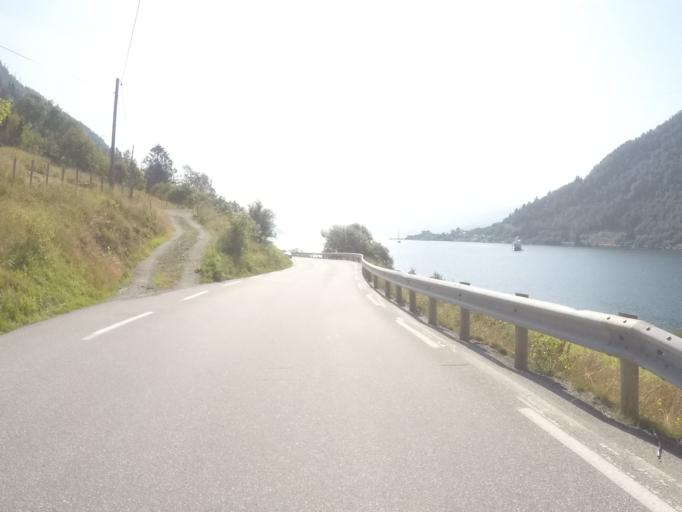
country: NO
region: Sogn og Fjordane
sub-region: Balestrand
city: Balestrand
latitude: 61.2198
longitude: 6.5045
